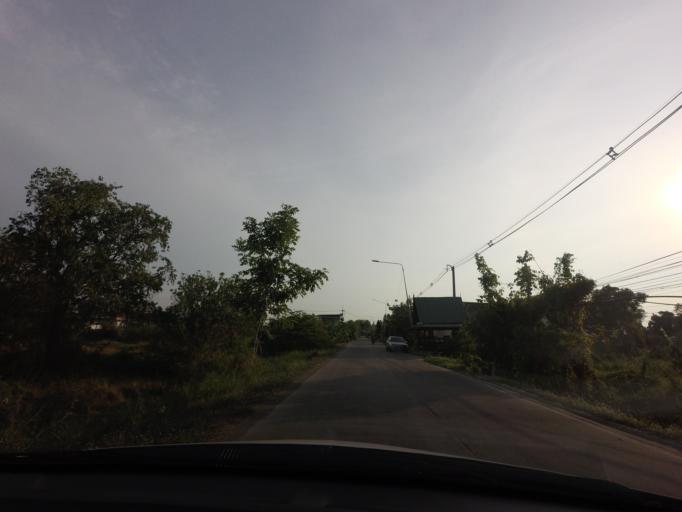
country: TH
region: Pathum Thani
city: Pathum Thani
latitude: 14.0333
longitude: 100.5416
